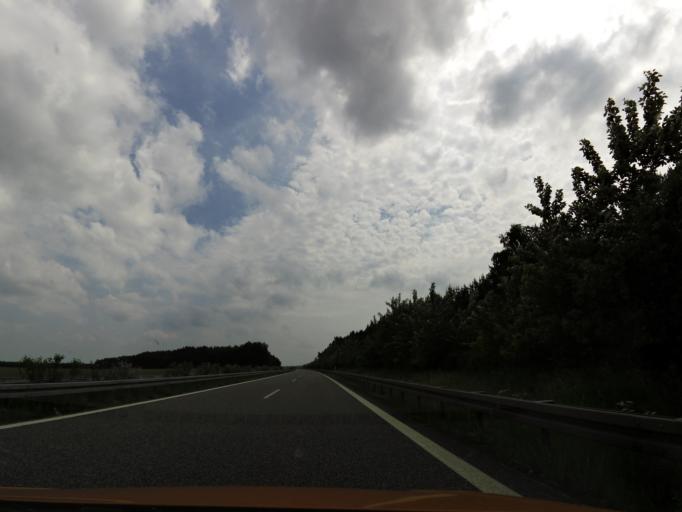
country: DE
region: Mecklenburg-Vorpommern
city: Mirow
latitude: 53.4926
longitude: 11.4790
